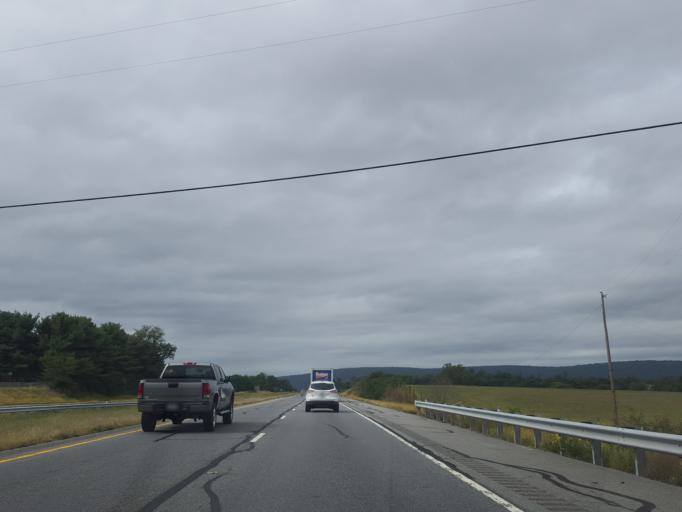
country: US
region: Maryland
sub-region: Frederick County
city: Brunswick
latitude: 39.3545
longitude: -77.6003
